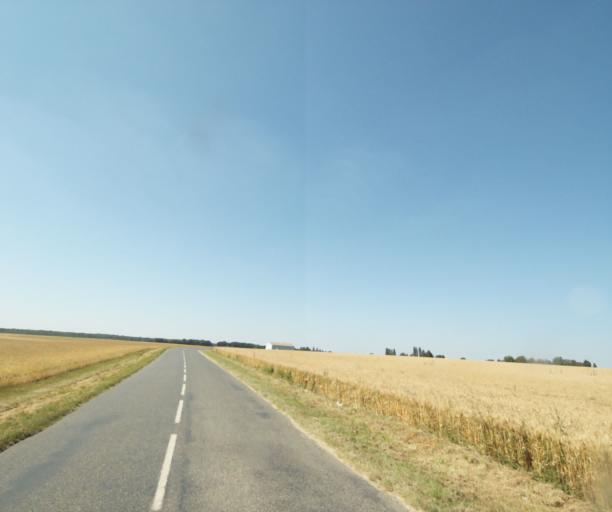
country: FR
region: Ile-de-France
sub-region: Departement de Seine-et-Marne
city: Acheres-la-Foret
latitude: 48.3363
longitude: 2.5619
